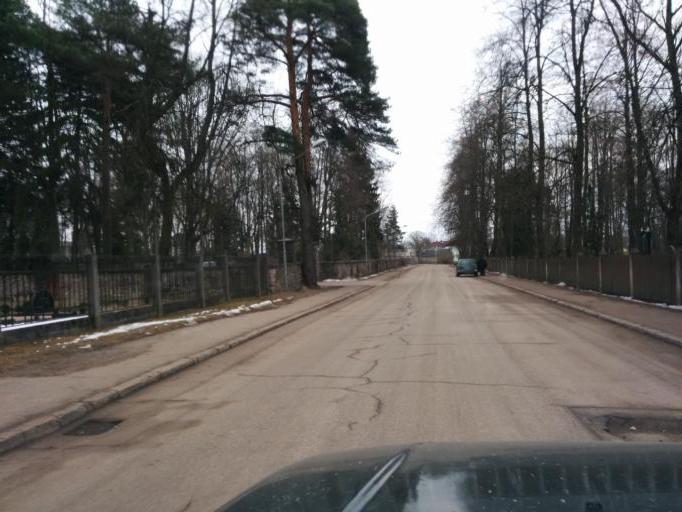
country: LV
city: Tireli
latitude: 56.9467
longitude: 23.6245
